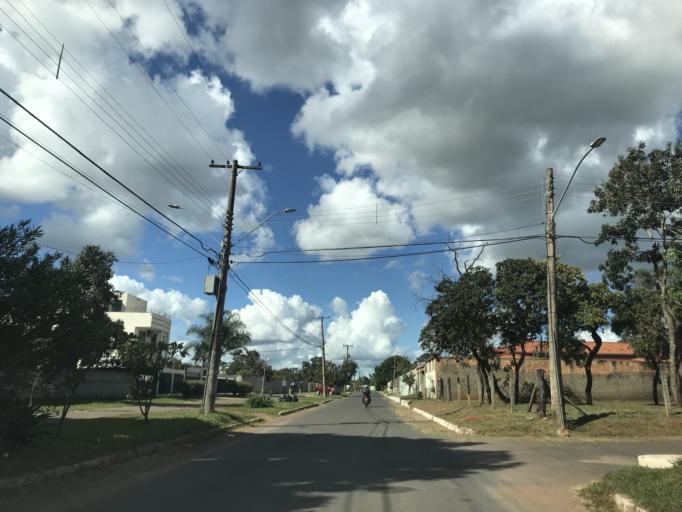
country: BR
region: Federal District
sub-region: Brasilia
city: Brasilia
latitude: -15.7400
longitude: -47.7514
